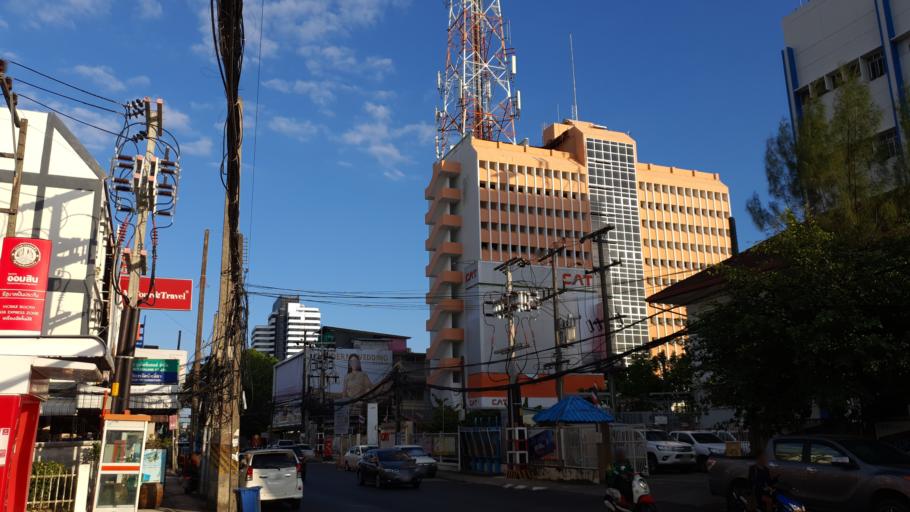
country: TH
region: Phuket
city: Ban Talat Nua
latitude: 7.8836
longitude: 98.3912
